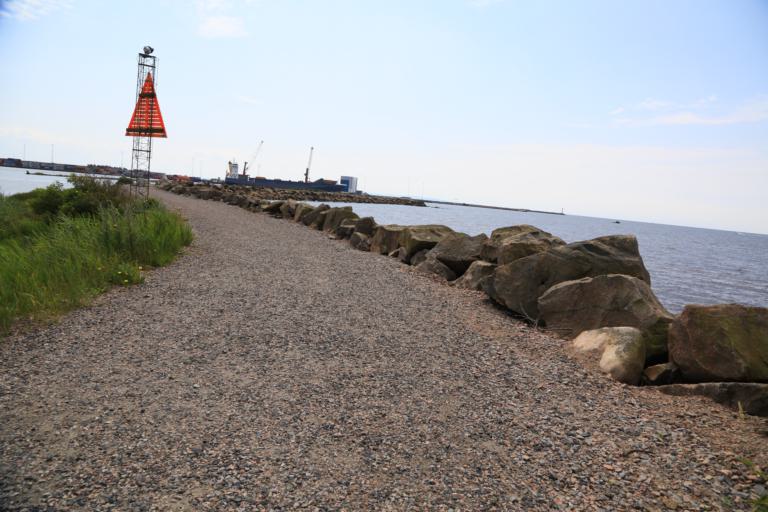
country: SE
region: Halland
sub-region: Halmstads Kommun
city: Halmstad
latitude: 56.6582
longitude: 12.8476
